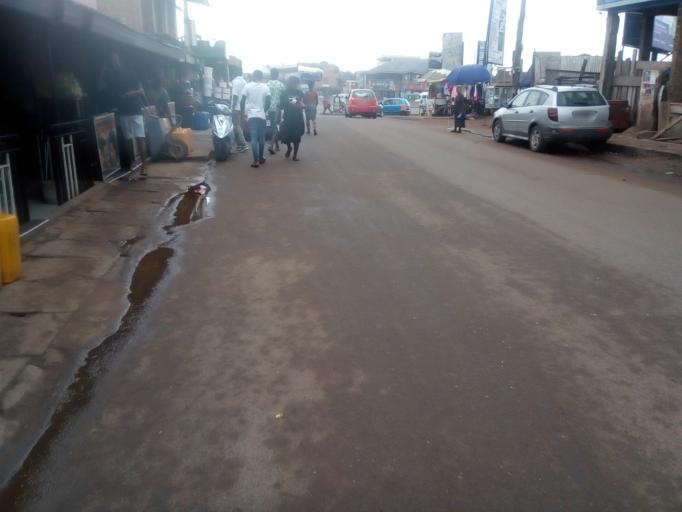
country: GH
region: Greater Accra
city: Dome
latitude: 5.6055
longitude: -0.2529
